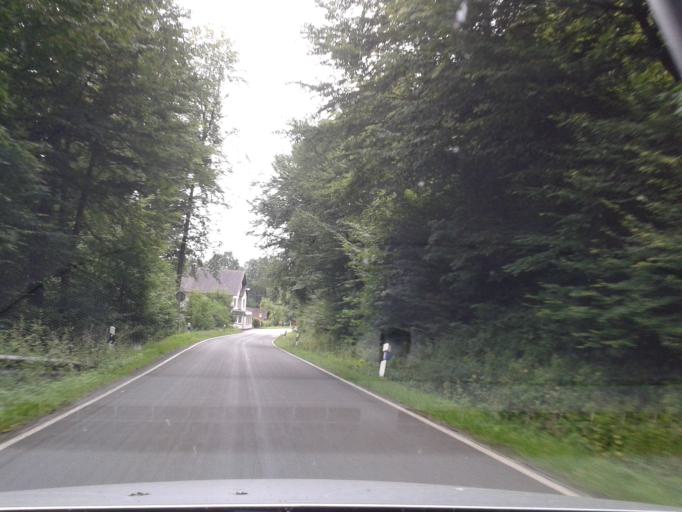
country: DE
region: North Rhine-Westphalia
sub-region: Regierungsbezirk Detmold
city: Barntrup
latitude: 51.9471
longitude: 9.1418
